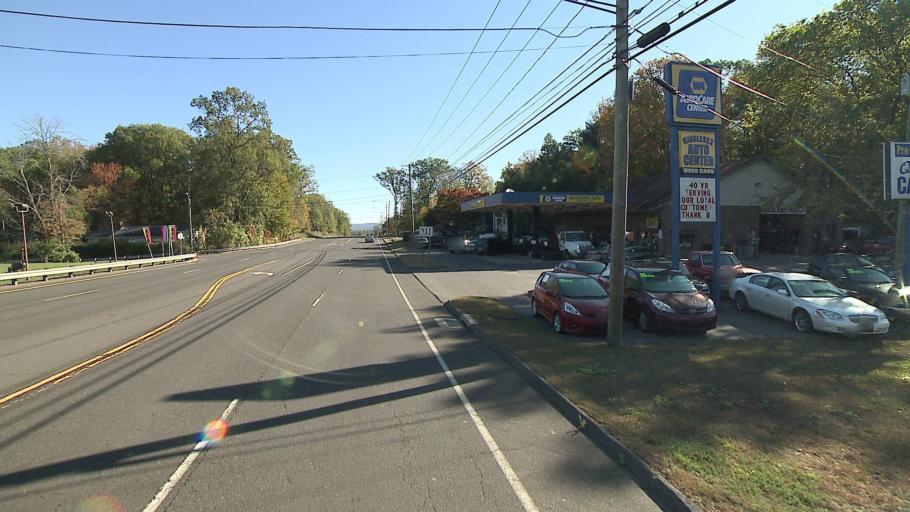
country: US
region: Connecticut
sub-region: Middlesex County
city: Middletown
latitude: 41.5483
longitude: -72.6980
